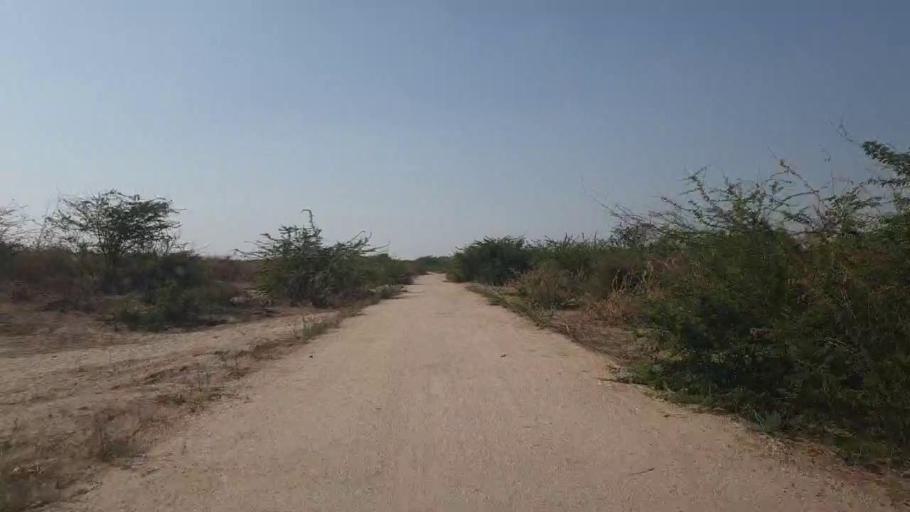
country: PK
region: Sindh
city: Dhoro Naro
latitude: 25.4976
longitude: 69.6255
